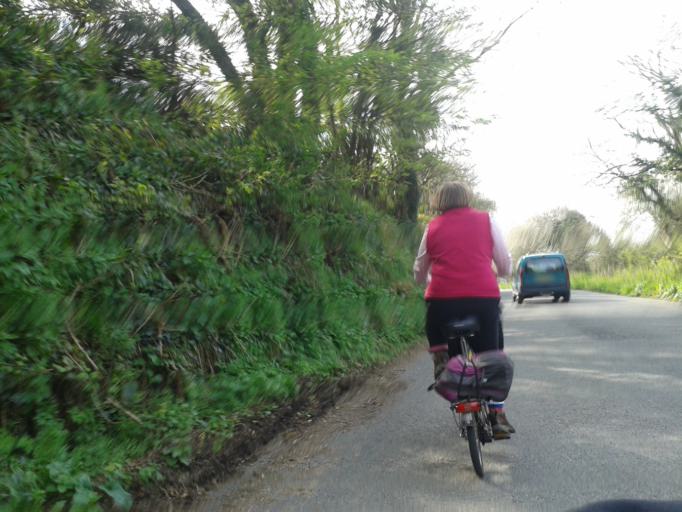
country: GB
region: England
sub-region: Devon
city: Braunton
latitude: 51.1309
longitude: -4.2084
